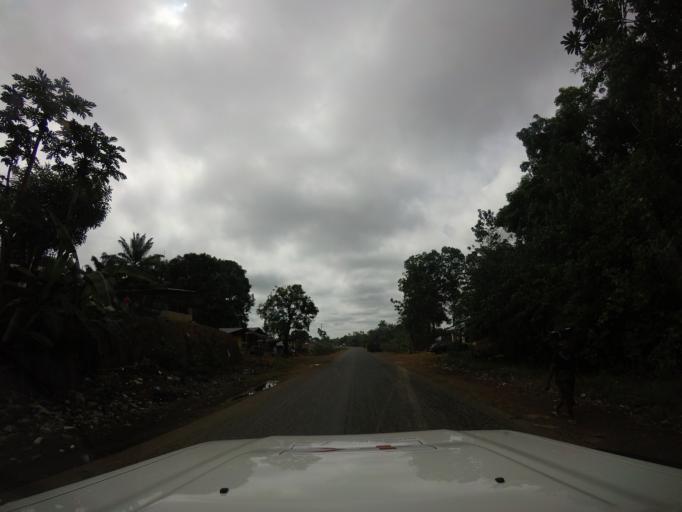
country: LR
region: Montserrado
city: Monrovia
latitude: 6.5389
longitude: -10.8555
